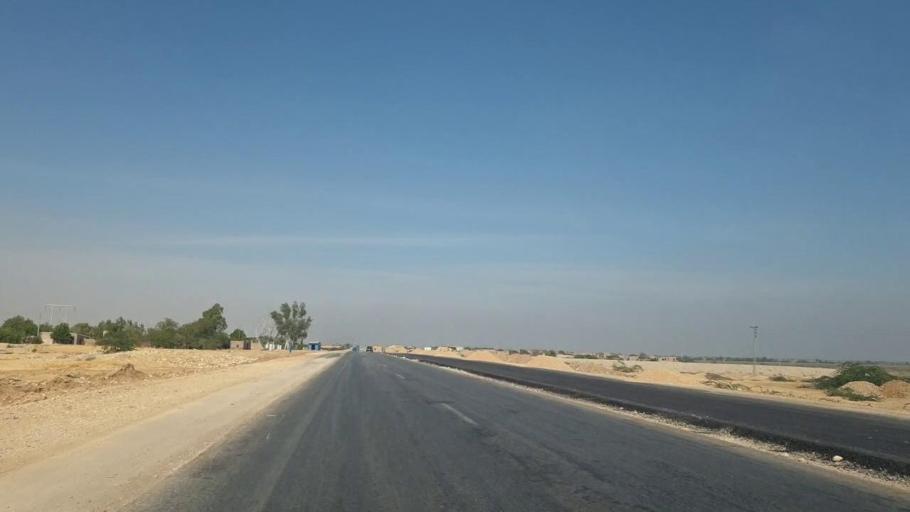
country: PK
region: Sindh
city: Matiari
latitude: 25.6641
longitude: 68.2954
